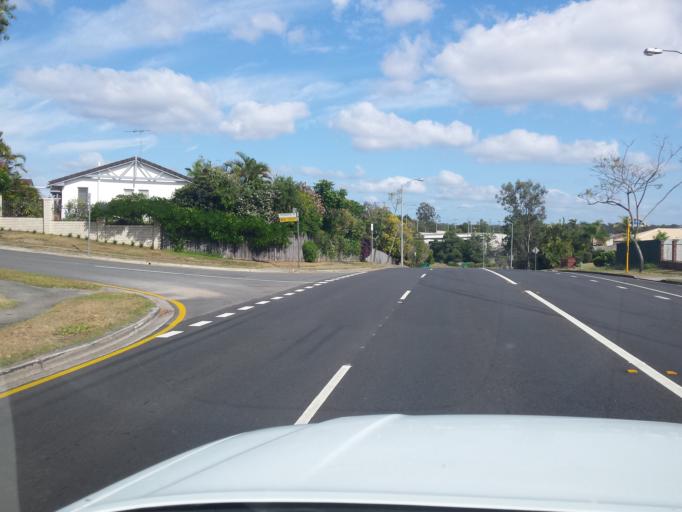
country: AU
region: Queensland
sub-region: Brisbane
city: Everton Park
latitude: -27.3872
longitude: 152.9868
